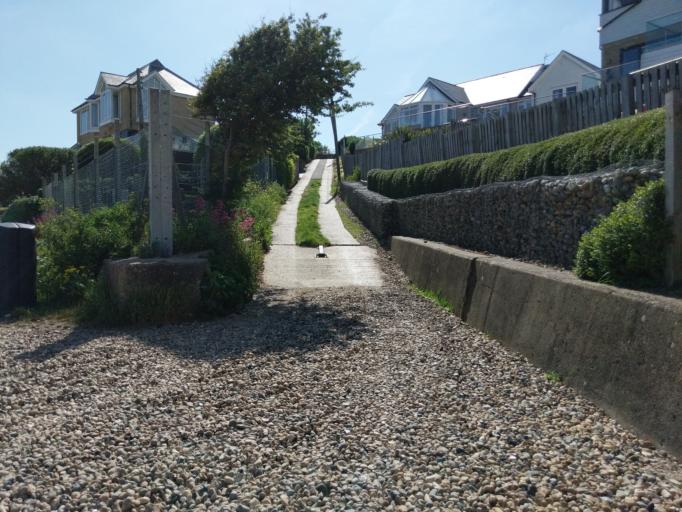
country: GB
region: England
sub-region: Kent
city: Whitstable
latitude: 51.3489
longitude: 1.0048
